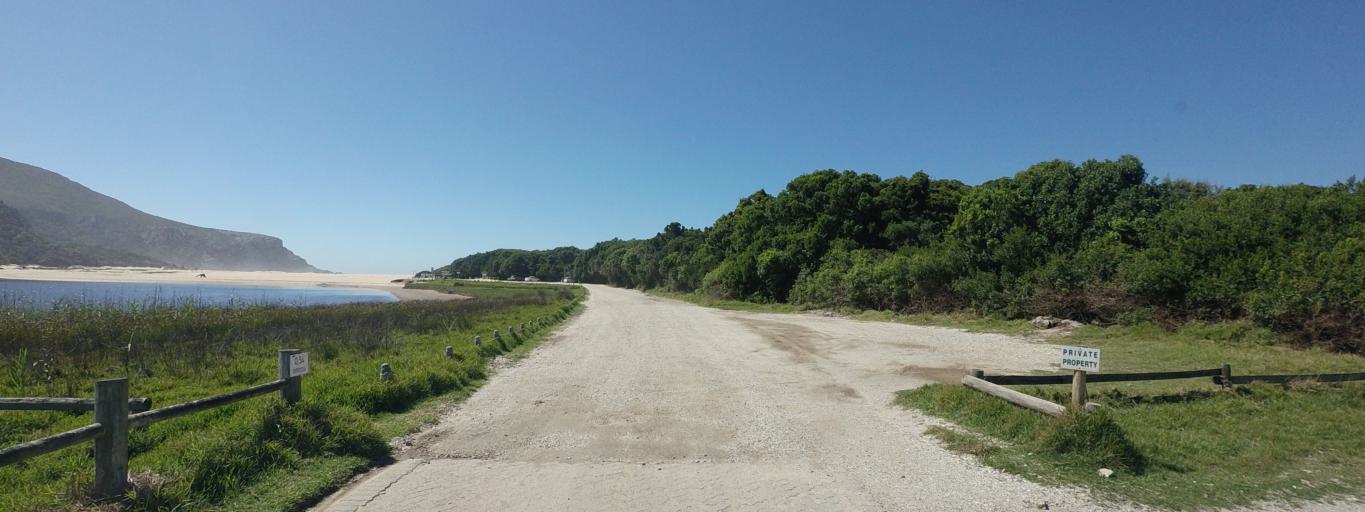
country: ZA
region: Western Cape
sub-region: Eden District Municipality
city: Plettenberg Bay
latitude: -33.9797
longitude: 23.5651
